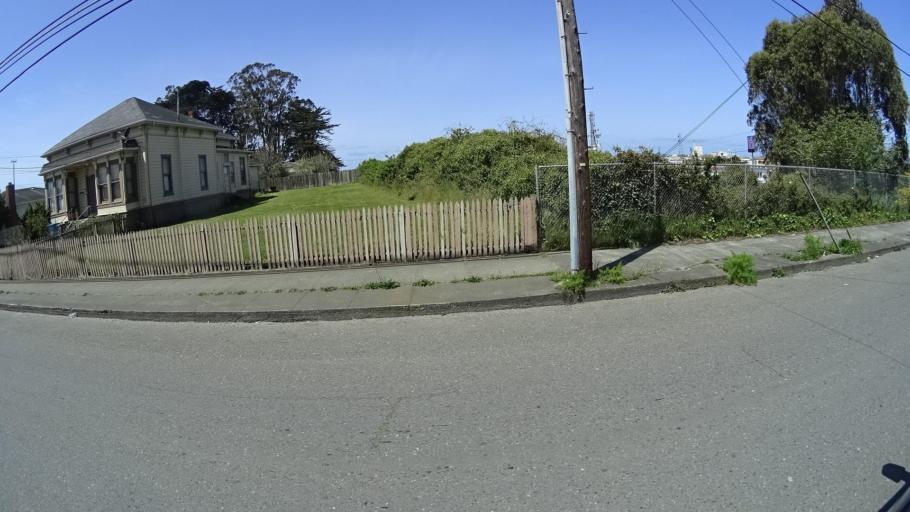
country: US
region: California
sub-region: Humboldt County
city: Bayview
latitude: 40.7886
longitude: -124.1784
